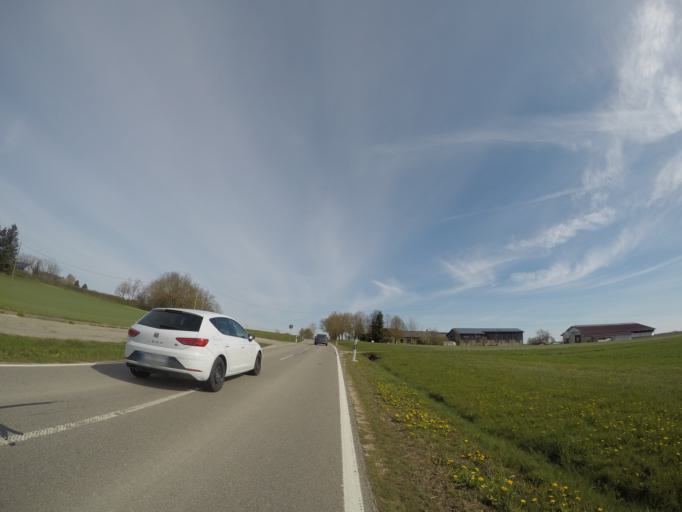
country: DE
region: Baden-Wuerttemberg
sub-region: Tuebingen Region
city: Laichingen
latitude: 48.5082
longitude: 9.6732
